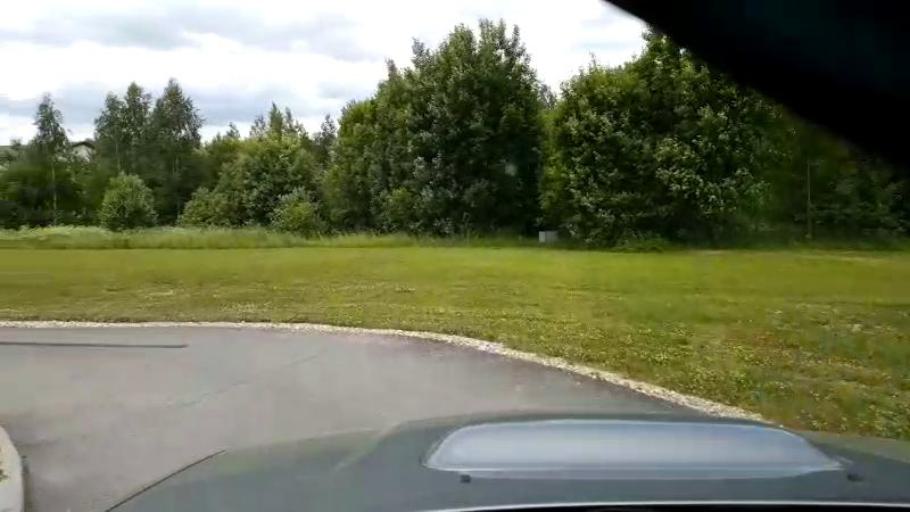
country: EE
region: Paernumaa
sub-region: Halinga vald
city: Parnu-Jaagupi
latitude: 58.5193
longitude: 24.5644
